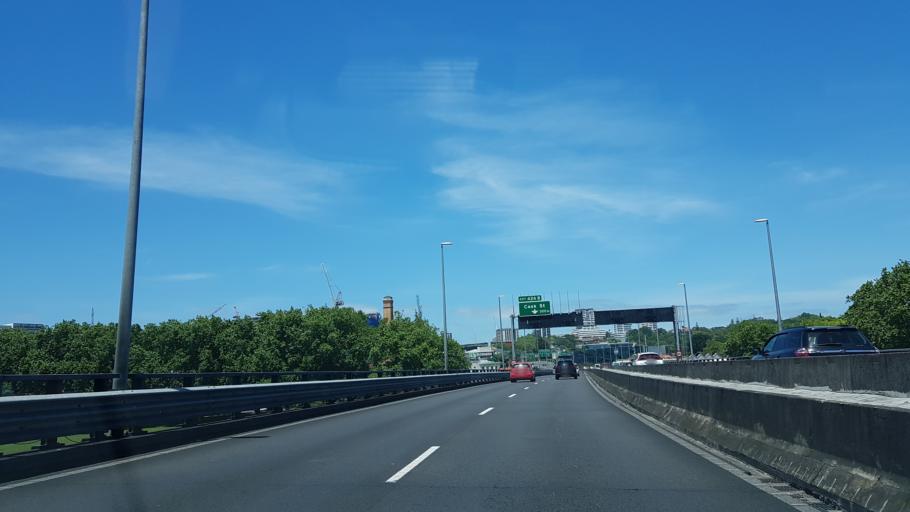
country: NZ
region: Auckland
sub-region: Auckland
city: Auckland
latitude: -36.8461
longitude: 174.7532
